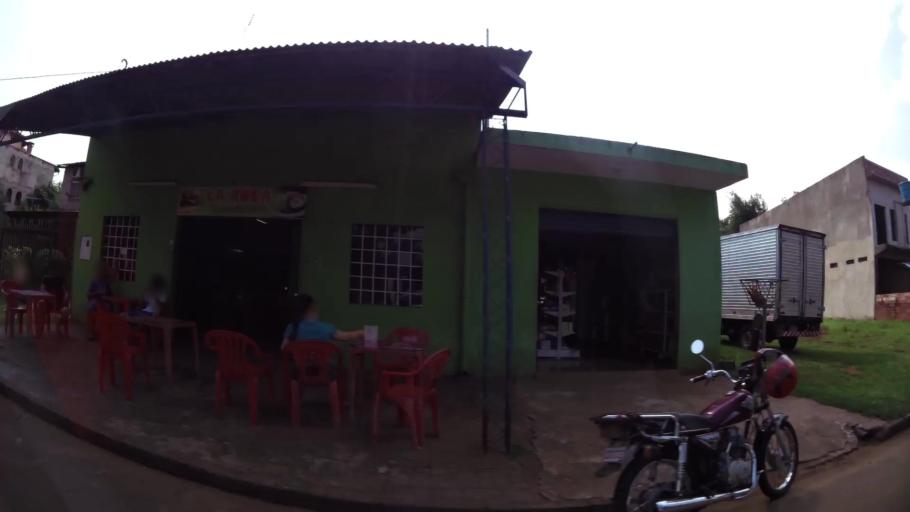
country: PY
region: Alto Parana
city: Ciudad del Este
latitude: -25.5059
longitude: -54.6270
